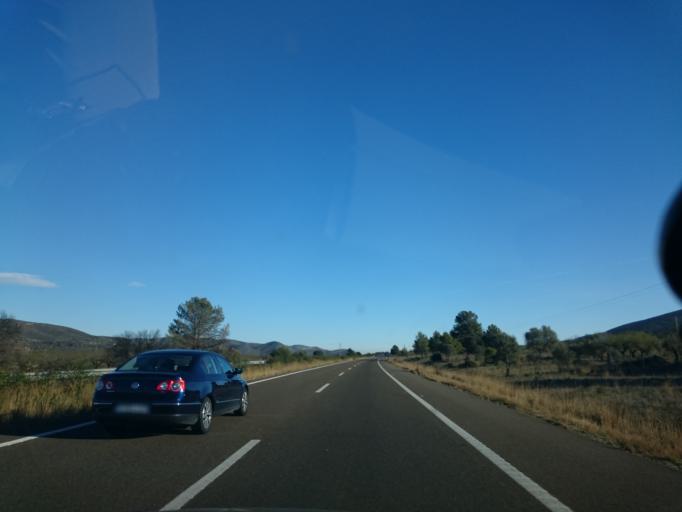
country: ES
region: Valencia
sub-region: Provincia de Castello
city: Alcala de Xivert
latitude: 40.3288
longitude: 0.2590
